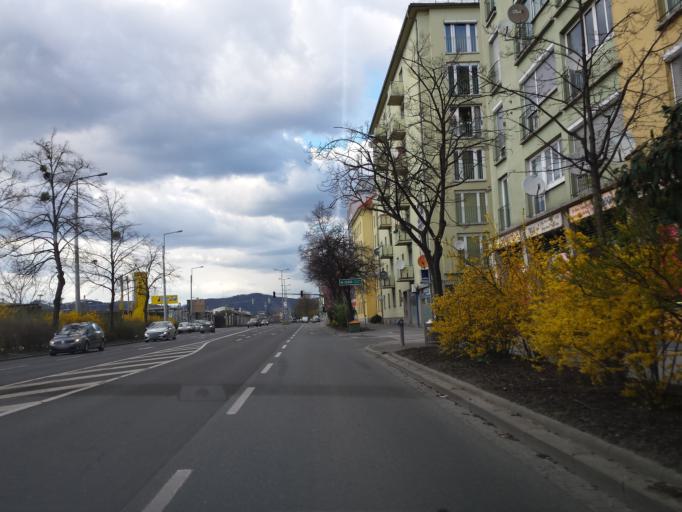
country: AT
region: Styria
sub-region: Graz Stadt
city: Wetzelsdorf
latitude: 47.0747
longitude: 15.4178
